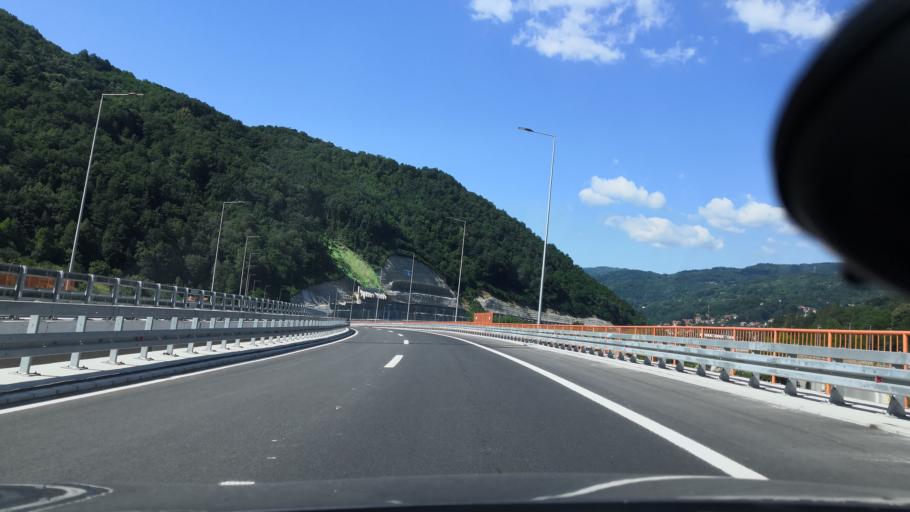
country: RS
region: Central Serbia
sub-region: Pcinjski Okrug
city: Vladicin Han
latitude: 42.8174
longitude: 22.1209
